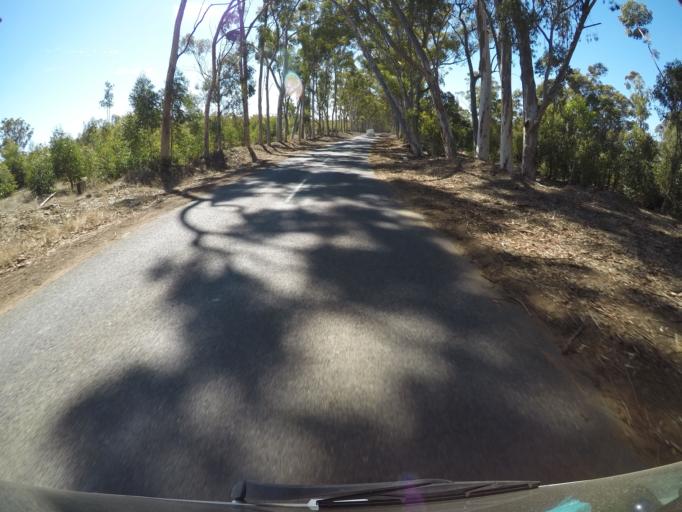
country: ZA
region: Western Cape
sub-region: City of Cape Town
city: Sunset Beach
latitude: -33.7557
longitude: 18.5545
